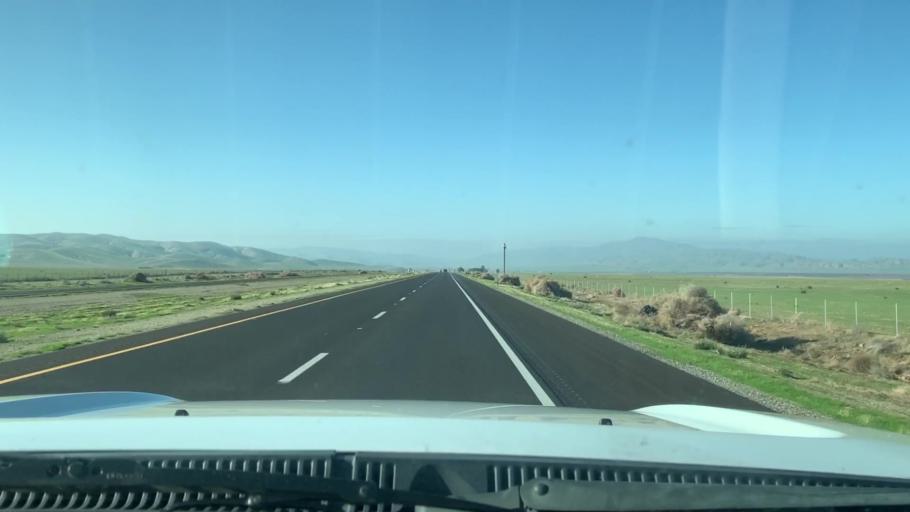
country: US
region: California
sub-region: Kern County
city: Lost Hills
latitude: 35.6293
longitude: -119.9953
